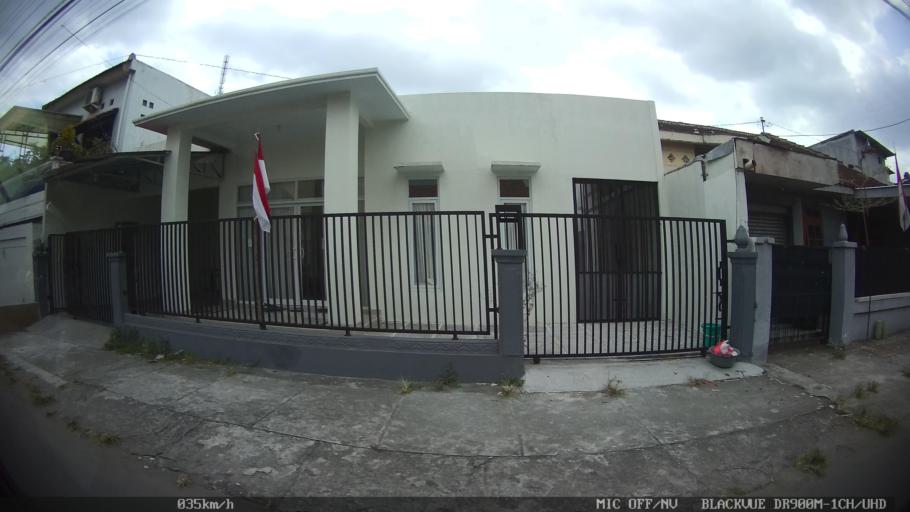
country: ID
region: Daerah Istimewa Yogyakarta
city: Yogyakarta
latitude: -7.7715
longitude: 110.3381
